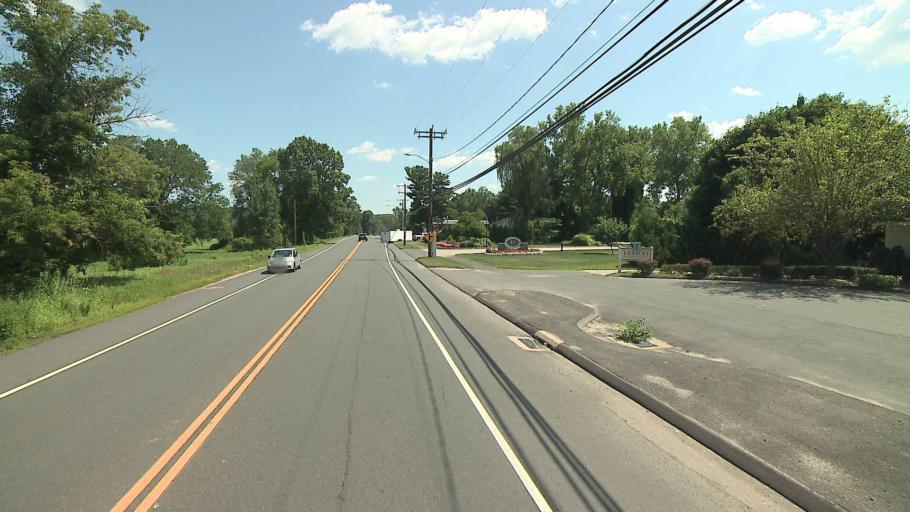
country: US
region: Connecticut
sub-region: Hartford County
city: Farmington
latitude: 41.7338
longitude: -72.8358
